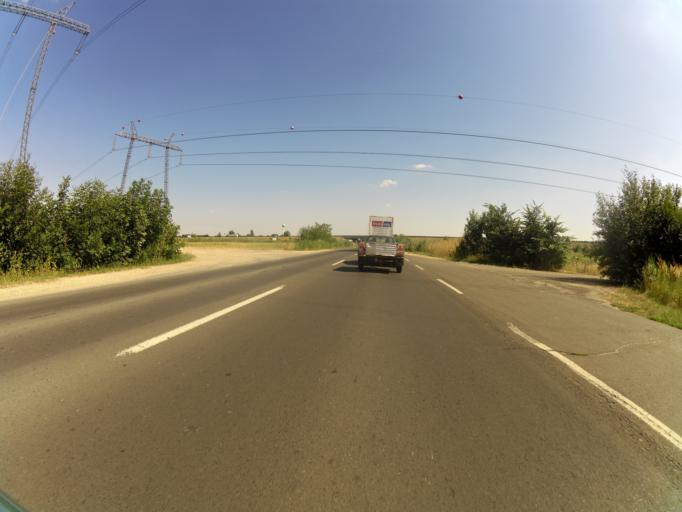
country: HU
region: Csongrad
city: Szatymaz
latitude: 46.2960
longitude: 20.0798
